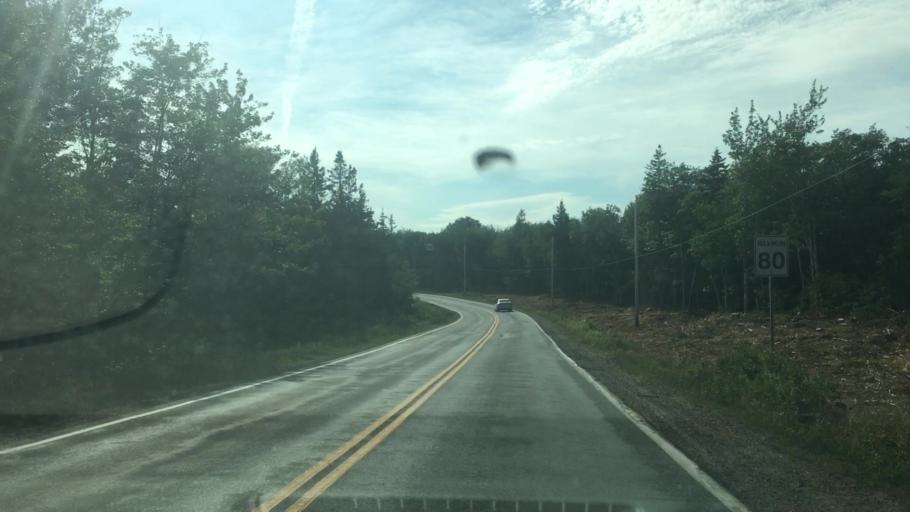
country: CA
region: Nova Scotia
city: Sydney Mines
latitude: 46.8818
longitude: -60.5124
